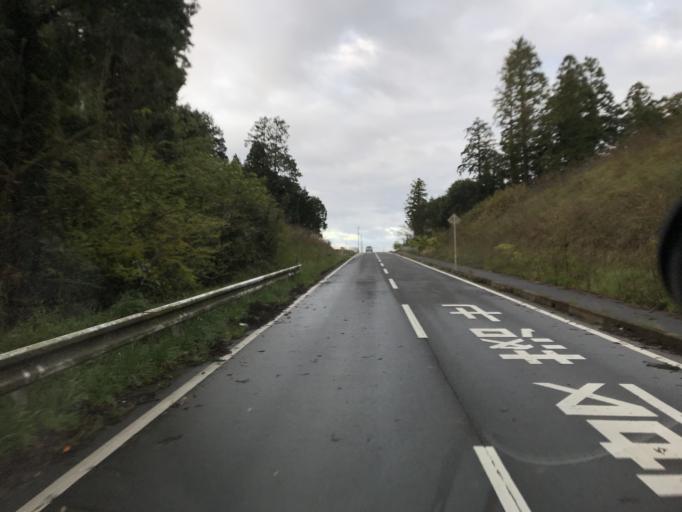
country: JP
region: Chiba
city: Yokaichiba
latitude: 35.7630
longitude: 140.4639
